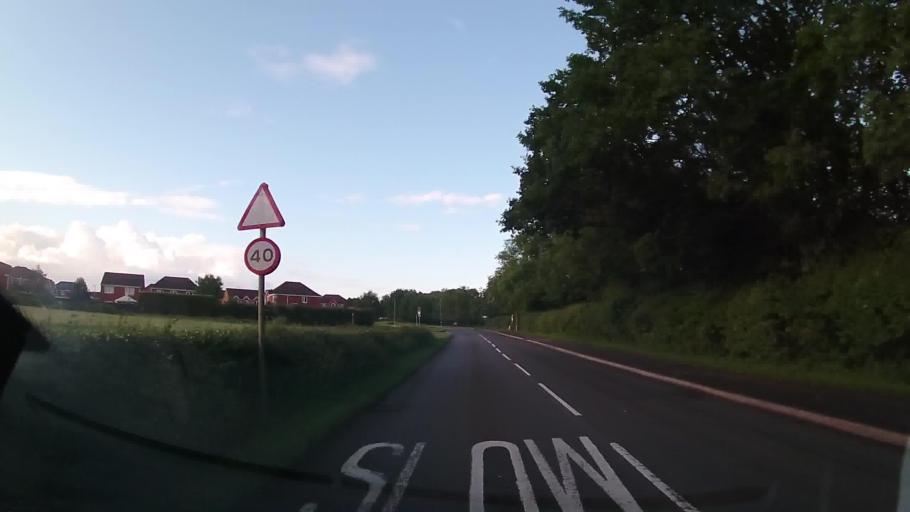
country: GB
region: England
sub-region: Leicestershire
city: Markfield
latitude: 52.6799
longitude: -1.2697
